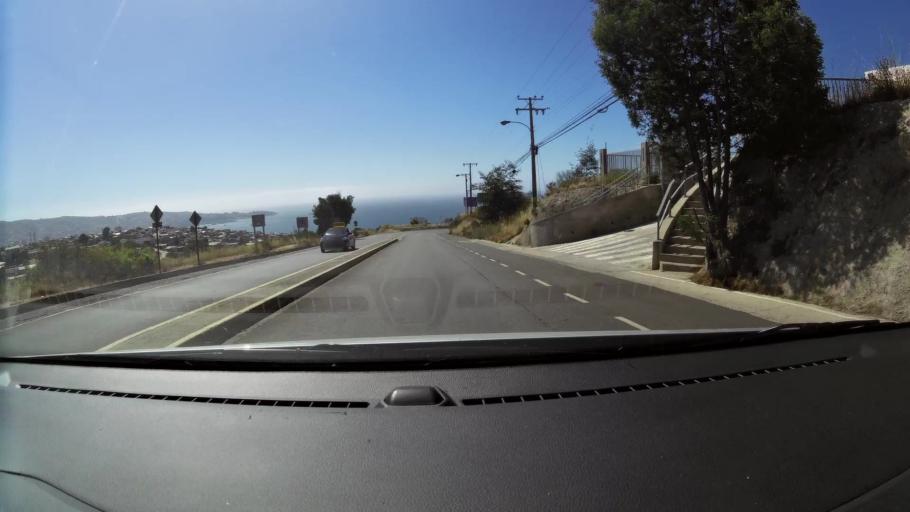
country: CL
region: Valparaiso
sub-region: Provincia de Valparaiso
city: Vina del Mar
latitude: -33.0397
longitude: -71.5702
